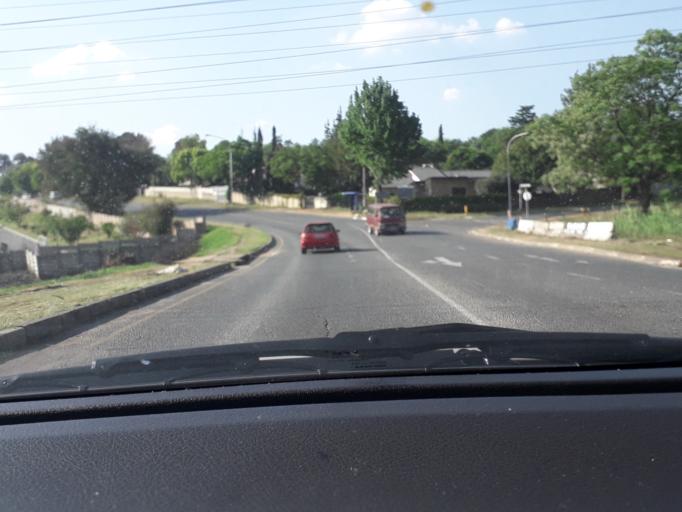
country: ZA
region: Gauteng
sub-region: City of Johannesburg Metropolitan Municipality
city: Modderfontein
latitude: -26.1271
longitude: 28.1243
